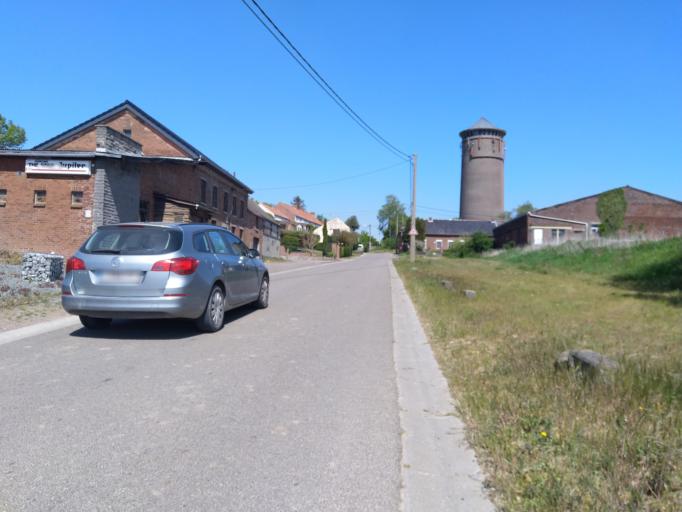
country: BE
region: Wallonia
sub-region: Province du Hainaut
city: Enghien
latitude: 50.6302
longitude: 4.0184
